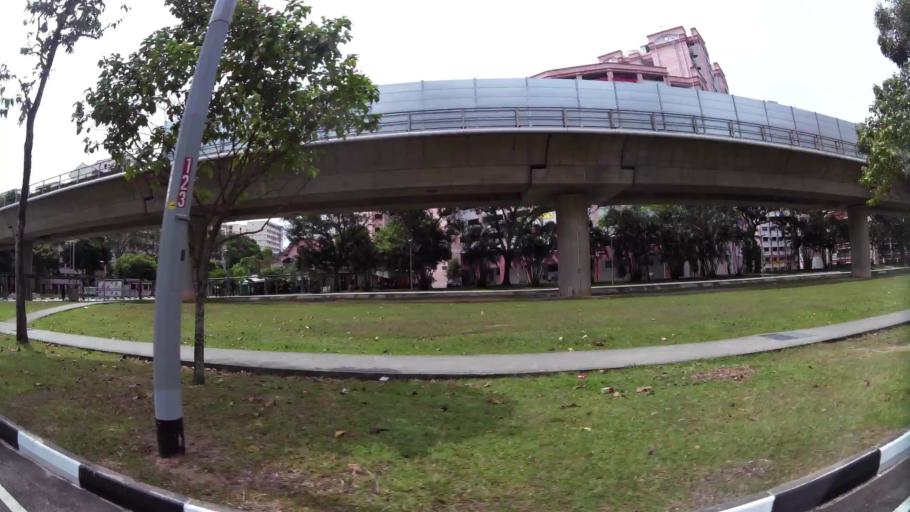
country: MY
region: Johor
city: Johor Bahru
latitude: 1.4010
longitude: 103.7486
